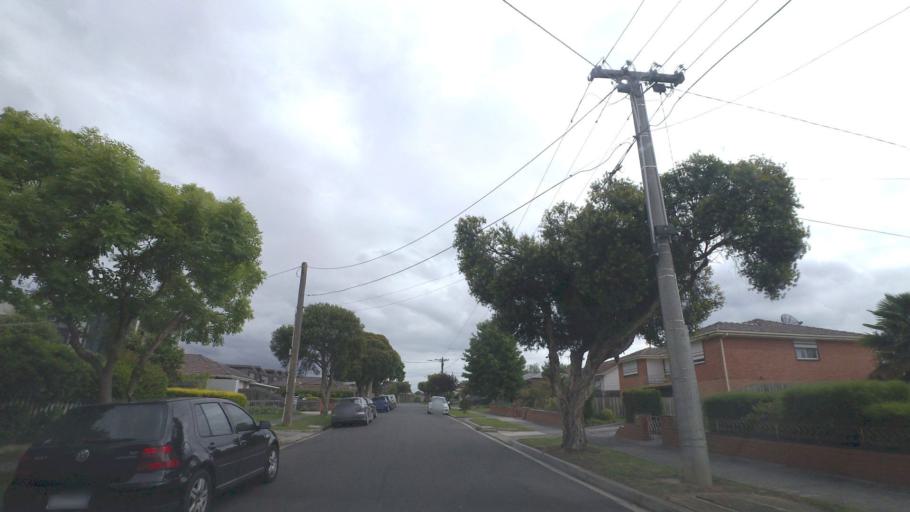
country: AU
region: Victoria
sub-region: Yarra Ranges
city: Lilydale
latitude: -37.7521
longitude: 145.3425
